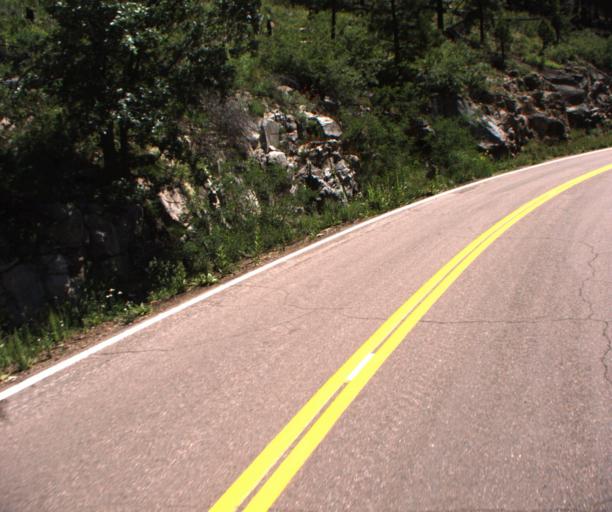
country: US
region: Arizona
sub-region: Greenlee County
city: Morenci
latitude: 33.5718
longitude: -109.3474
